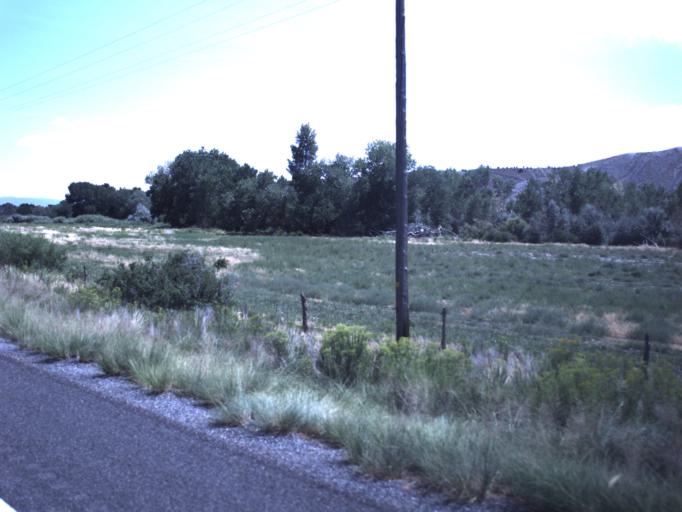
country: US
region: Utah
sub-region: Emery County
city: Huntington
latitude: 39.3539
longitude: -111.0175
